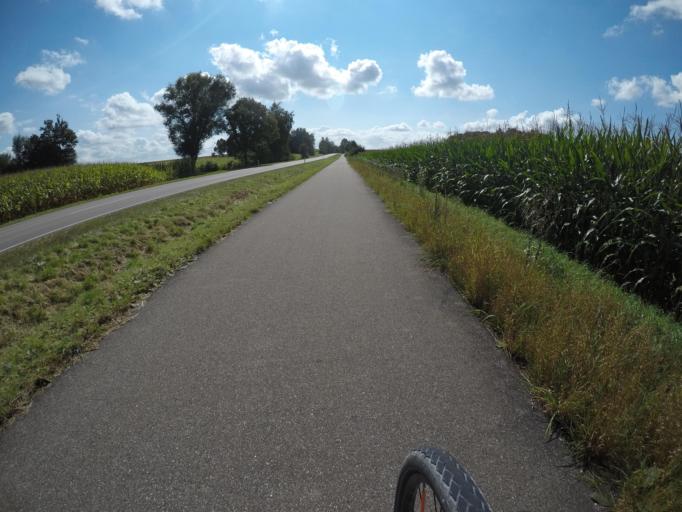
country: DE
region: Bavaria
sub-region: Swabia
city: Dillingen an der Donau
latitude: 48.6134
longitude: 10.5030
